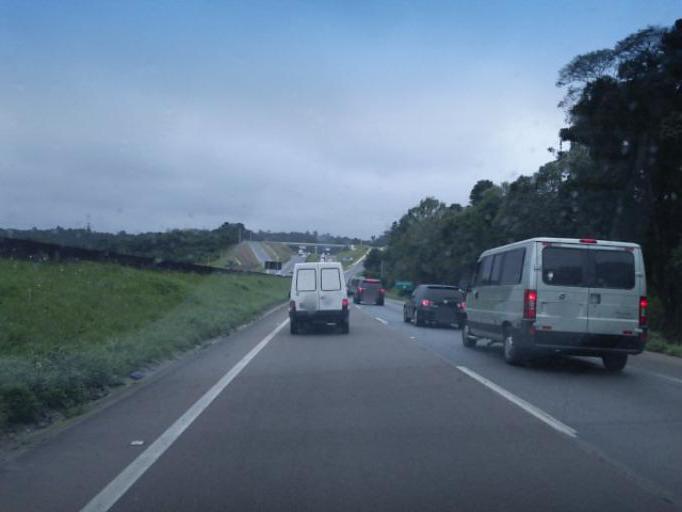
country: BR
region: Parana
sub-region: Sao Jose Dos Pinhais
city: Sao Jose dos Pinhais
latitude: -25.7734
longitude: -49.1213
